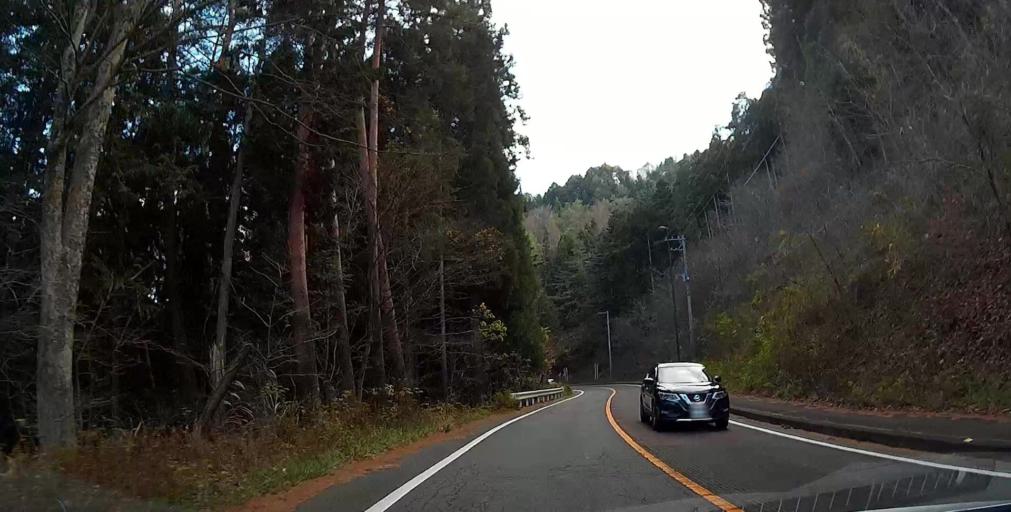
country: JP
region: Yamanashi
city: Fujikawaguchiko
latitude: 35.4786
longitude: 138.8315
